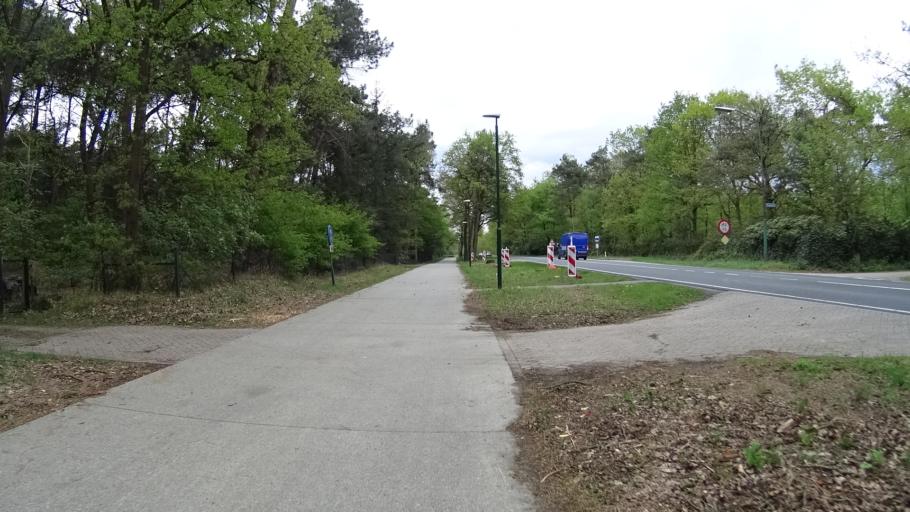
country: NL
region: North Brabant
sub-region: Gemeente Nuenen, Gerwen en Nederwetten
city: Nuenen
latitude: 51.5067
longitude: 5.5758
